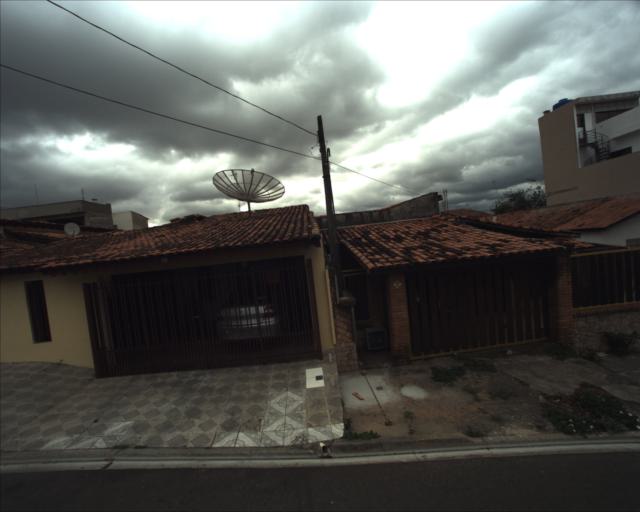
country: BR
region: Sao Paulo
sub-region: Sorocaba
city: Sorocaba
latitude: -23.4366
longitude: -47.5075
